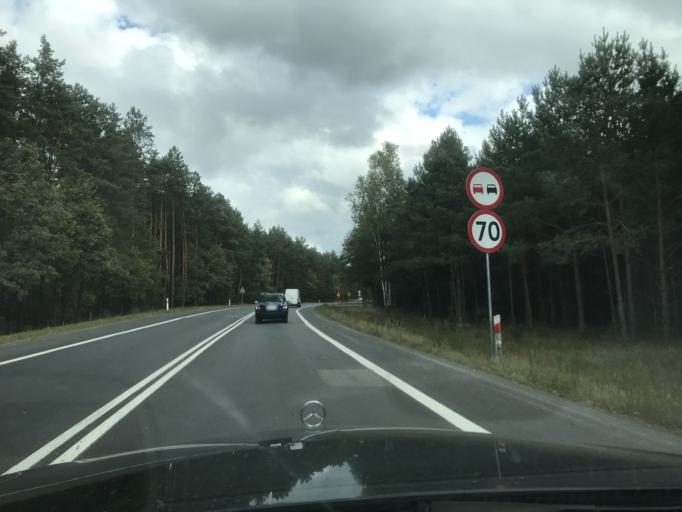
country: PL
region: Subcarpathian Voivodeship
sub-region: Powiat nizanski
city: Jarocin
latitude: 50.5990
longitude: 22.2769
